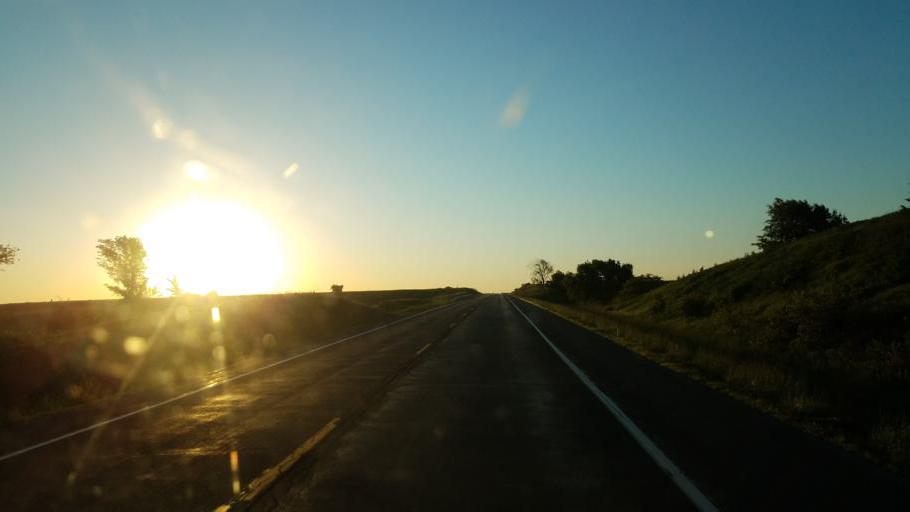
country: US
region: Missouri
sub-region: Schuyler County
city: Lancaster
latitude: 40.4926
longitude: -92.5882
